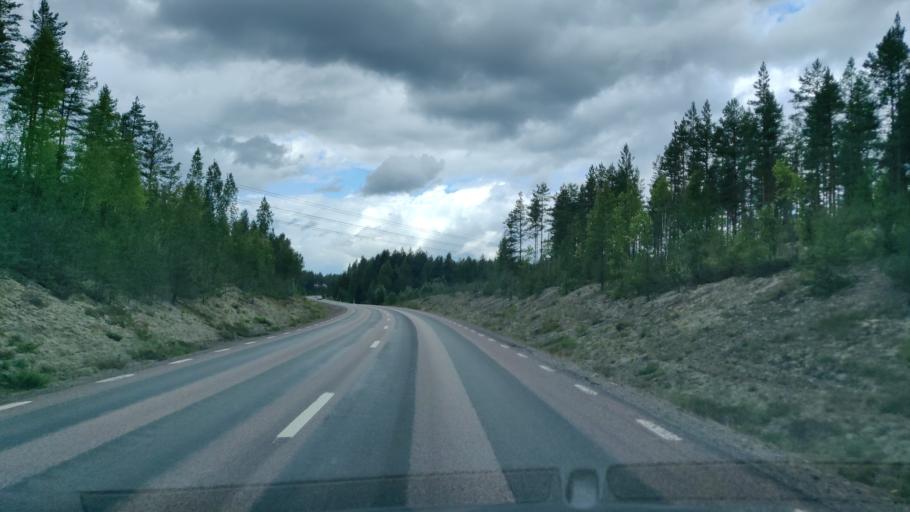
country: SE
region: Vaermland
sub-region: Torsby Kommun
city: Torsby
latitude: 60.5296
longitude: 13.1294
